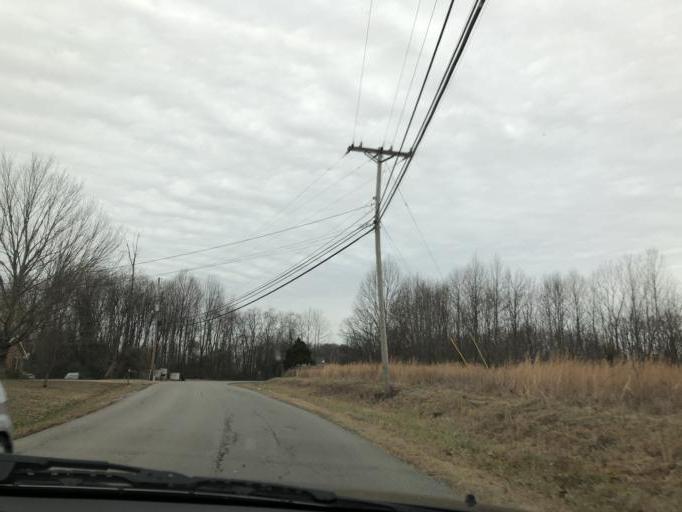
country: US
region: Tennessee
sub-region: Sumner County
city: Millersville
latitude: 36.4265
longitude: -86.6905
